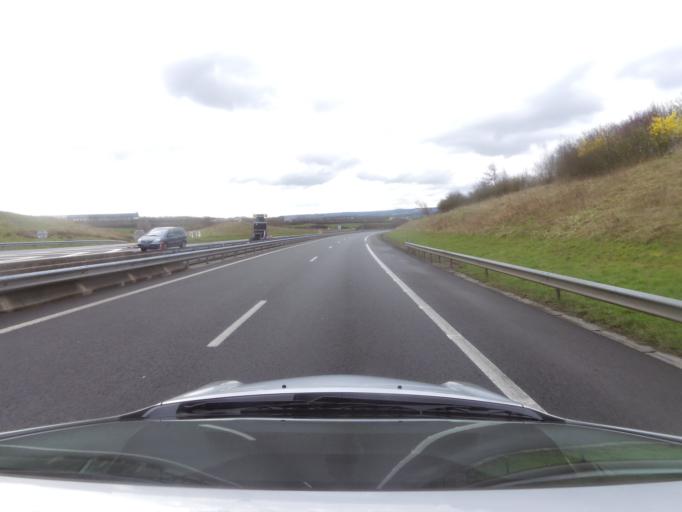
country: FR
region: Nord-Pas-de-Calais
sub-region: Departement du Pas-de-Calais
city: Isques
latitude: 50.6770
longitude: 1.6628
